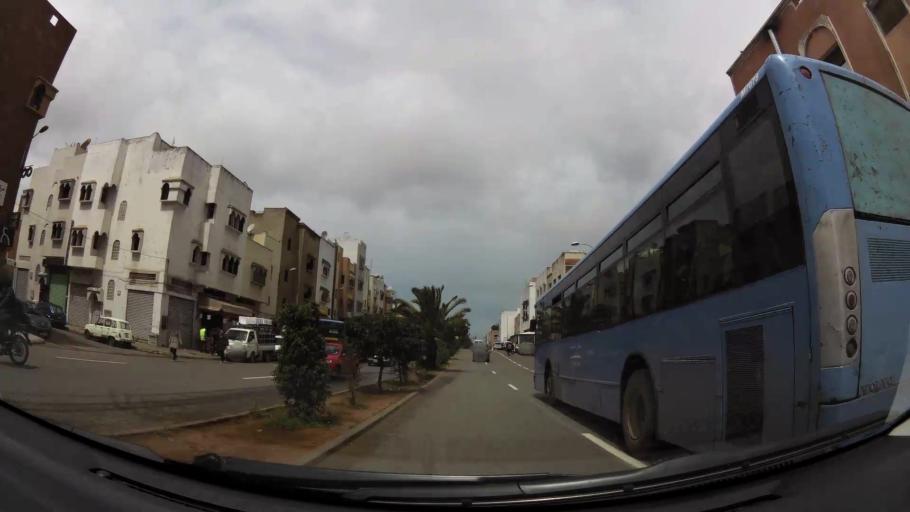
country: MA
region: Grand Casablanca
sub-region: Casablanca
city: Casablanca
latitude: 33.5508
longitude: -7.6842
